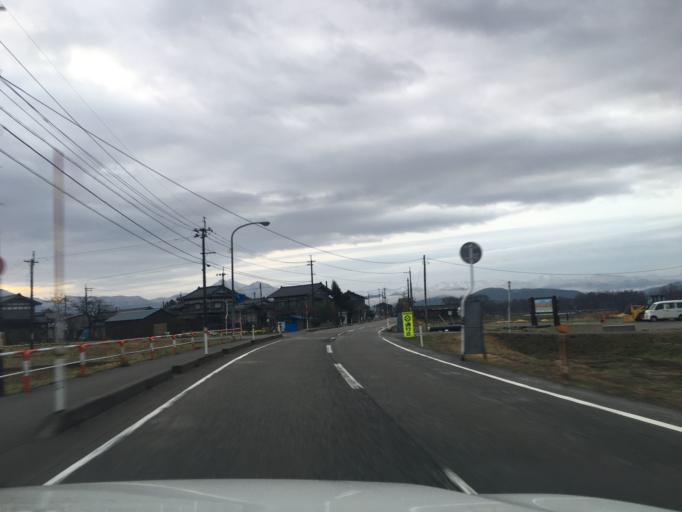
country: JP
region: Niigata
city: Murakami
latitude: 38.2759
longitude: 139.5237
